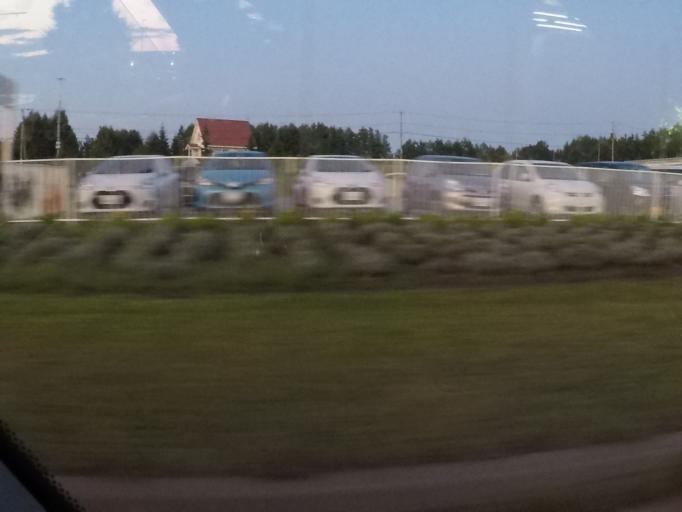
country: JP
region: Hokkaido
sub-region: Asahikawa-shi
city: Asahikawa
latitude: 43.6696
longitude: 142.4582
